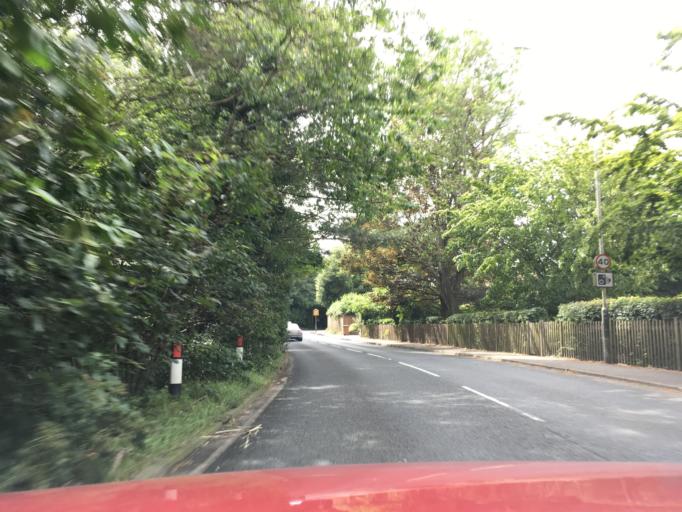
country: GB
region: England
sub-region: Kent
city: Royal Tunbridge Wells
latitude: 51.1305
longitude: 0.2173
